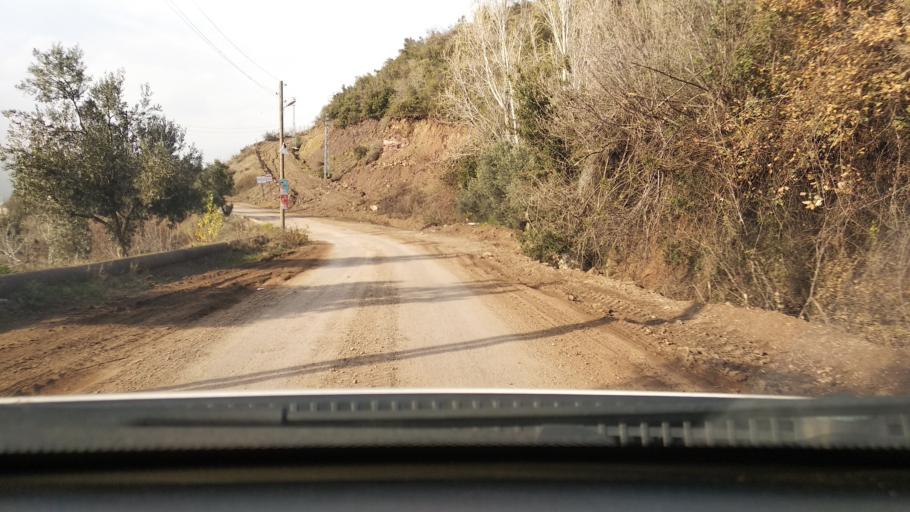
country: TR
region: Mersin
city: Kuzucubelen
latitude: 36.8713
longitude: 34.4684
